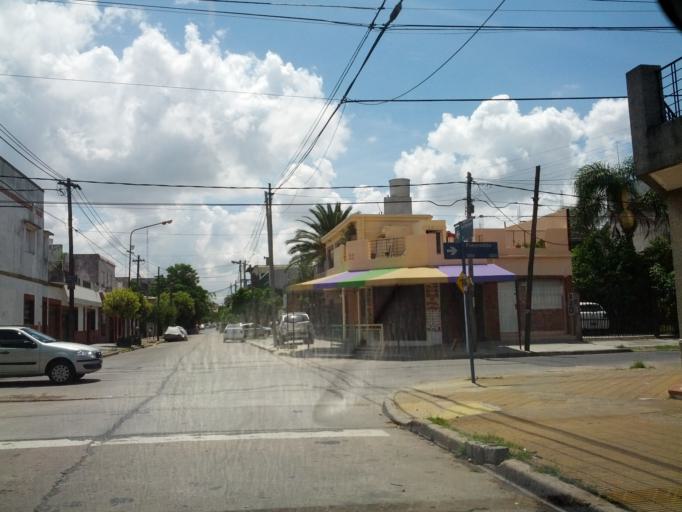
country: AR
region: Buenos Aires
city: San Justo
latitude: -34.6499
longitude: -58.5533
